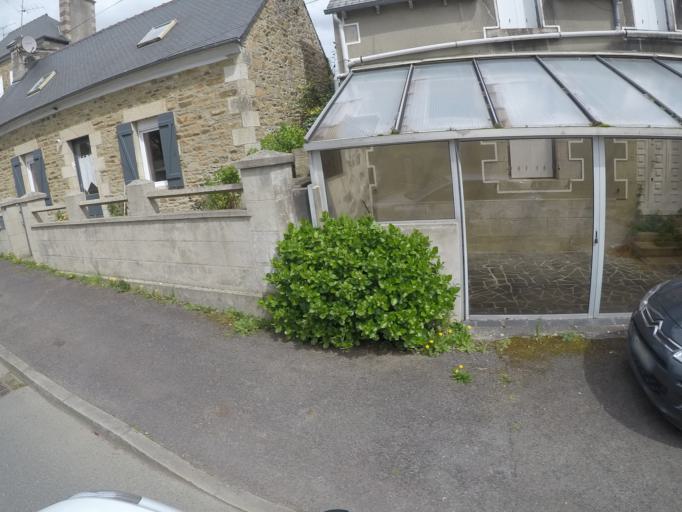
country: FR
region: Brittany
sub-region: Departement des Cotes-d'Armor
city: Plouha
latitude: 48.6729
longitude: -2.9262
